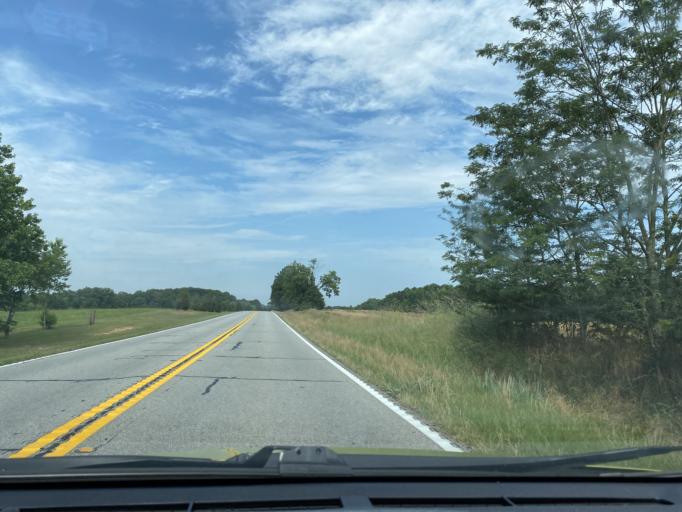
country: US
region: Georgia
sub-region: Coweta County
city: Senoia
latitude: 33.3029
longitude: -84.6655
